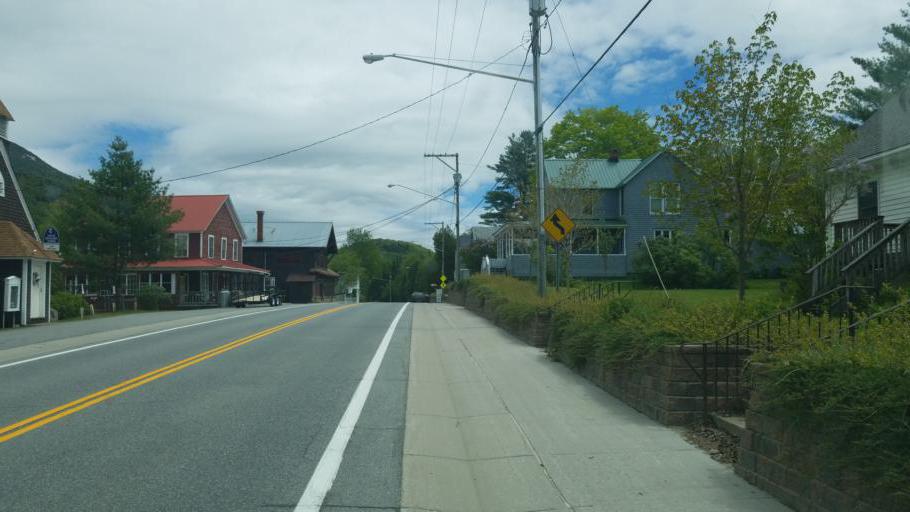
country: US
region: New York
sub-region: Franklin County
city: Tupper Lake
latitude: 43.8543
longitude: -74.4373
